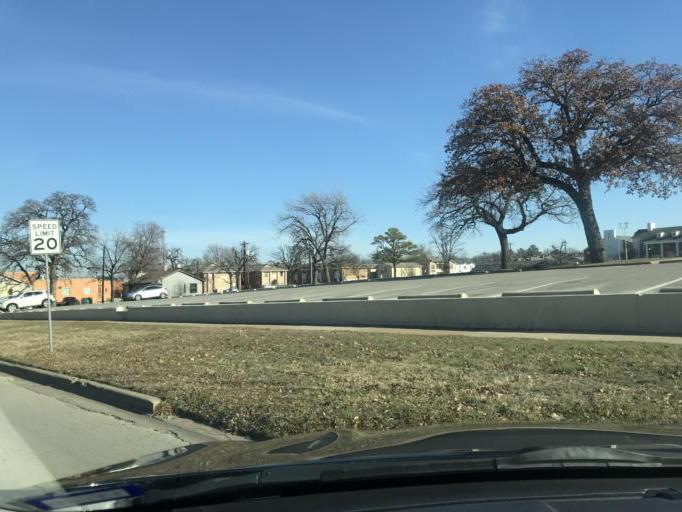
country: US
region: Texas
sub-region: Denton County
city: Denton
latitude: 33.2096
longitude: -97.1443
